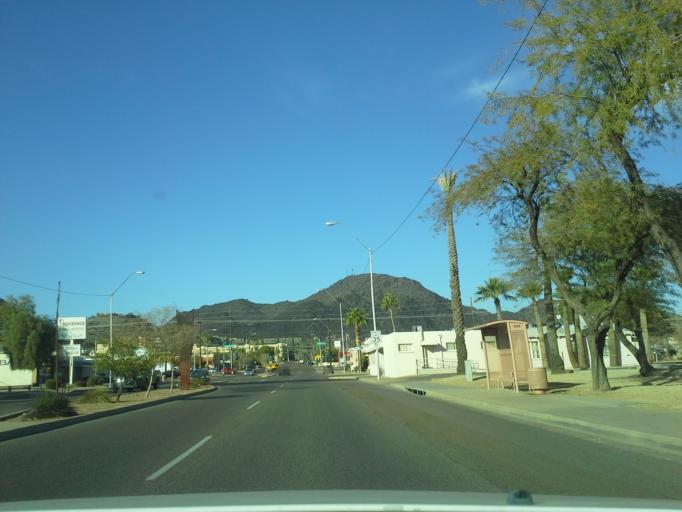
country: US
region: Arizona
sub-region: Maricopa County
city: Glendale
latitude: 33.5697
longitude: -112.0738
